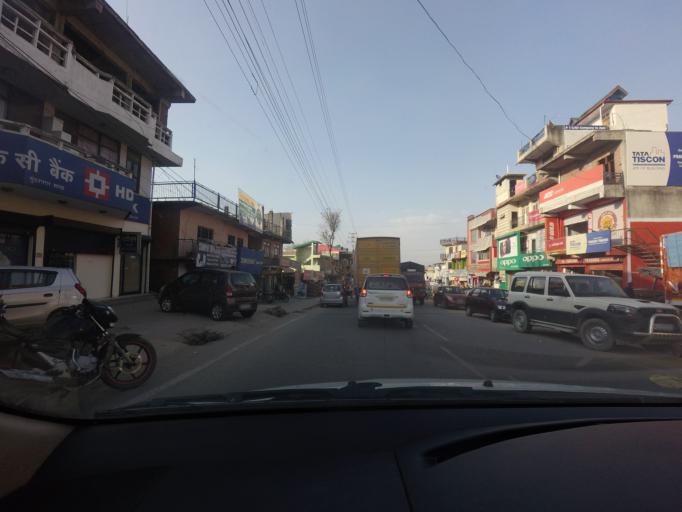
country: IN
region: Himachal Pradesh
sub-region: Mandi
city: Sundarnagar
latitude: 31.5310
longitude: 76.8881
